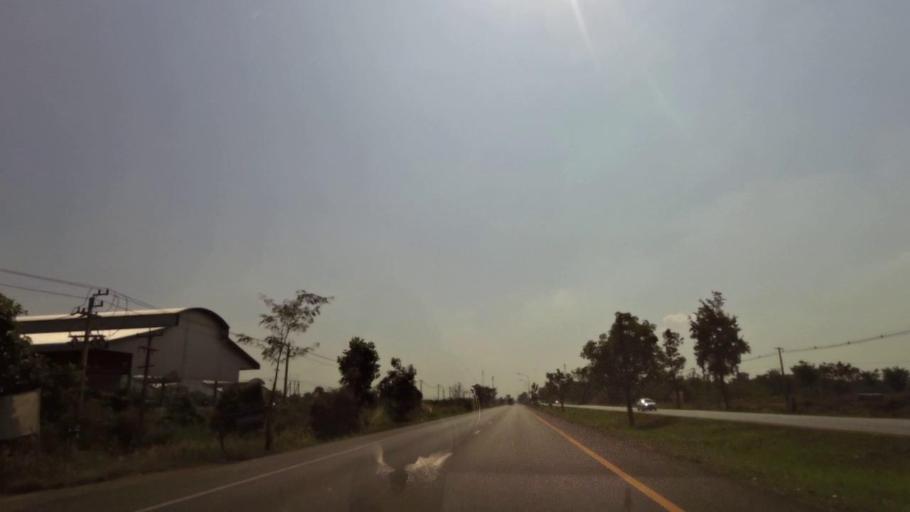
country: TH
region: Phichit
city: Bueng Na Rang
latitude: 16.2774
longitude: 100.1271
